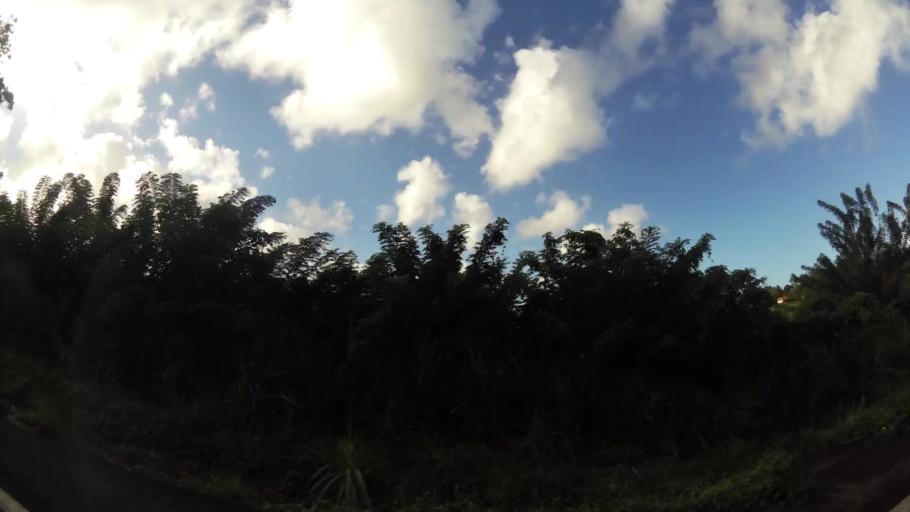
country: MQ
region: Martinique
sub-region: Martinique
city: Ducos
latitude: 14.6006
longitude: -60.9495
